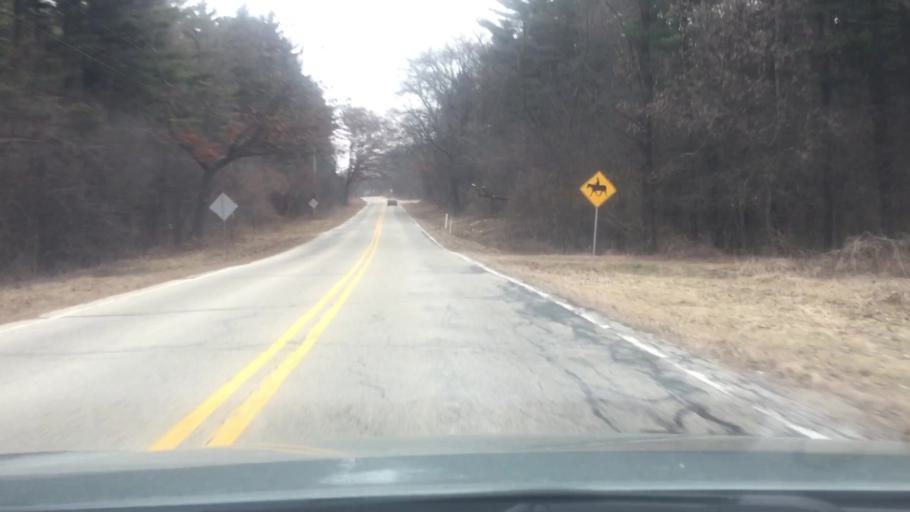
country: US
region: Wisconsin
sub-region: Waukesha County
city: North Prairie
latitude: 42.9419
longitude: -88.4373
